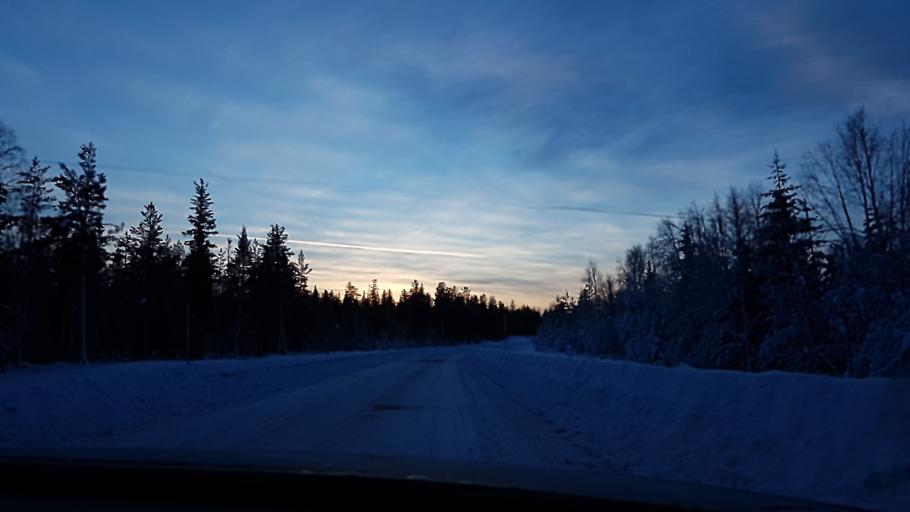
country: SE
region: Norrbotten
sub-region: Jokkmokks Kommun
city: Jokkmokk
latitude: 66.0827
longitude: 20.0734
